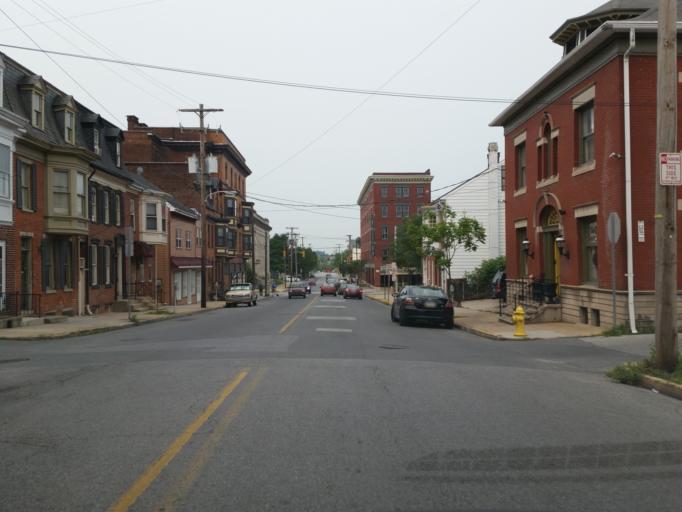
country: US
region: Pennsylvania
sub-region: York County
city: York
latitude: 39.9601
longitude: -76.7251
